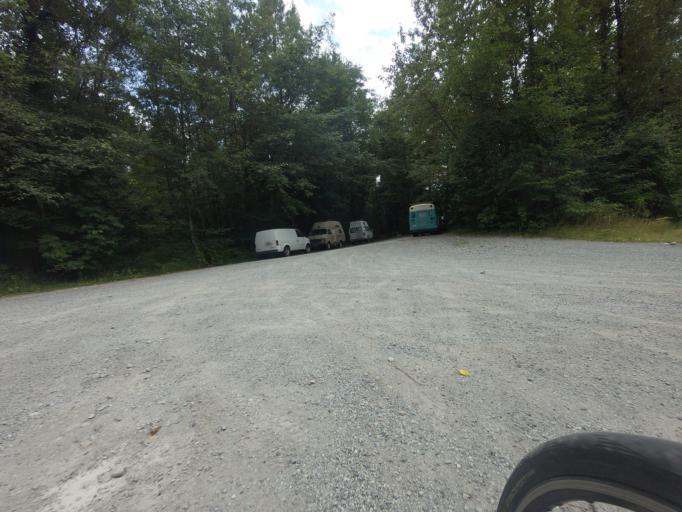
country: CA
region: British Columbia
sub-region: Greater Vancouver Regional District
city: Lions Bay
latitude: 49.7298
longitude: -123.1474
